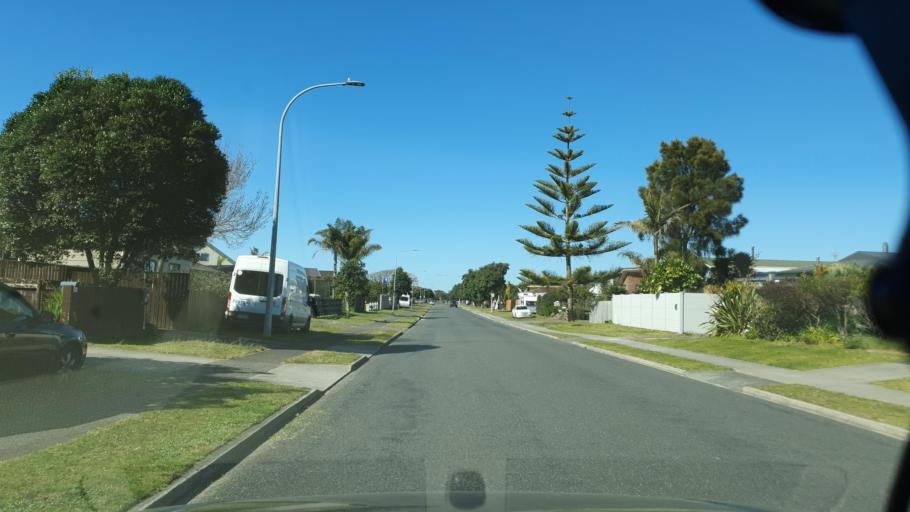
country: NZ
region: Bay of Plenty
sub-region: Tauranga City
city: Tauranga
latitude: -37.7031
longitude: 176.2972
